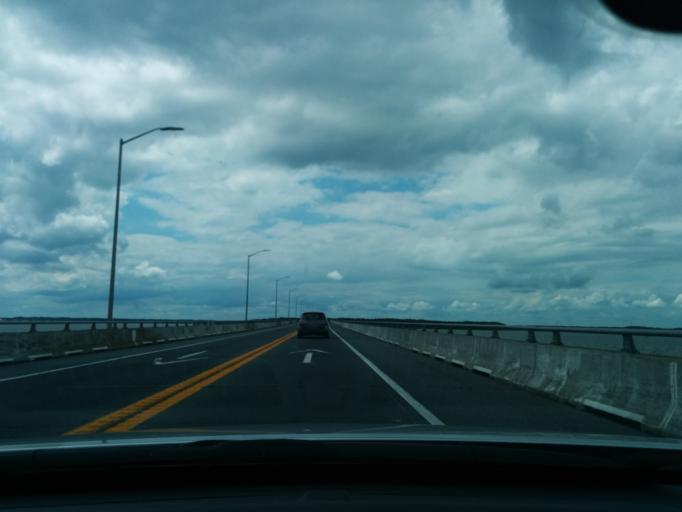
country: US
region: Maryland
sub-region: Worcester County
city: Ocean City
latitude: 38.3877
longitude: -75.0842
